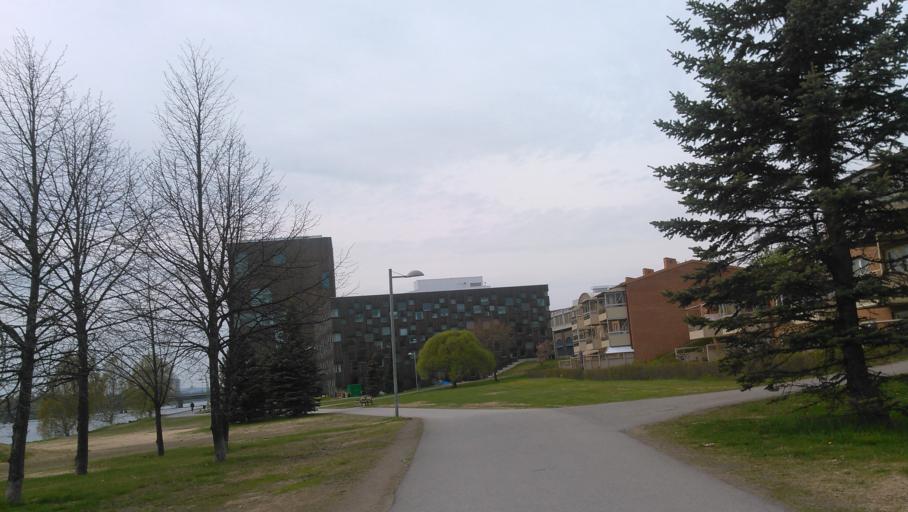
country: SE
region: Vaesterbotten
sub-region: Umea Kommun
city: Umea
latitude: 63.8196
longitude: 20.2800
